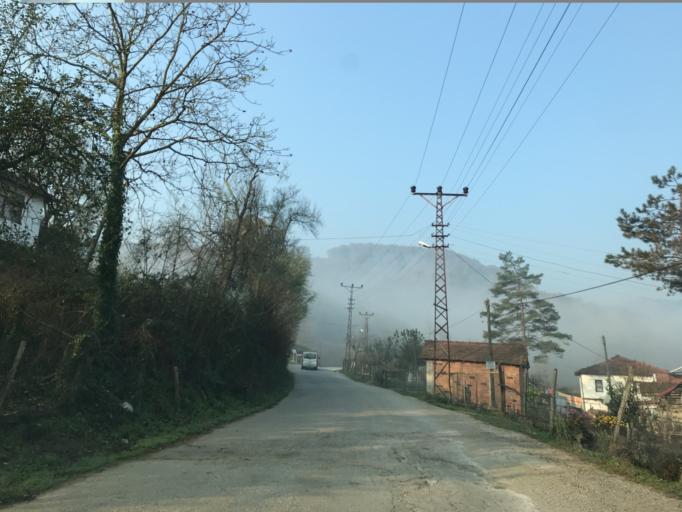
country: TR
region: Duzce
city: Cumayeri
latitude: 40.9130
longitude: 30.9422
